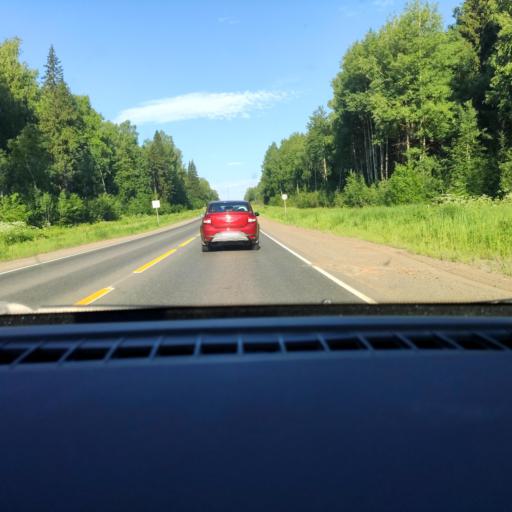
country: RU
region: Udmurtiya
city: Khokhryaki
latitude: 56.9161
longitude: 53.4361
